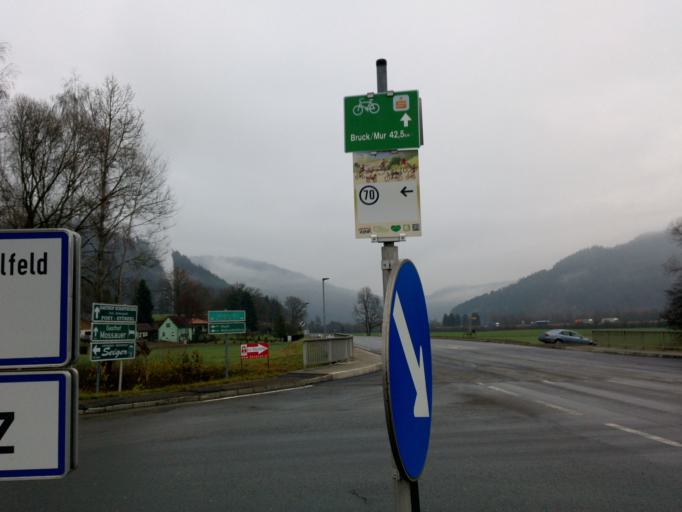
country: AT
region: Styria
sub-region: Politischer Bezirk Murtal
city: Feistritz bei Knittelfeld
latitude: 47.2626
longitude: 14.9036
